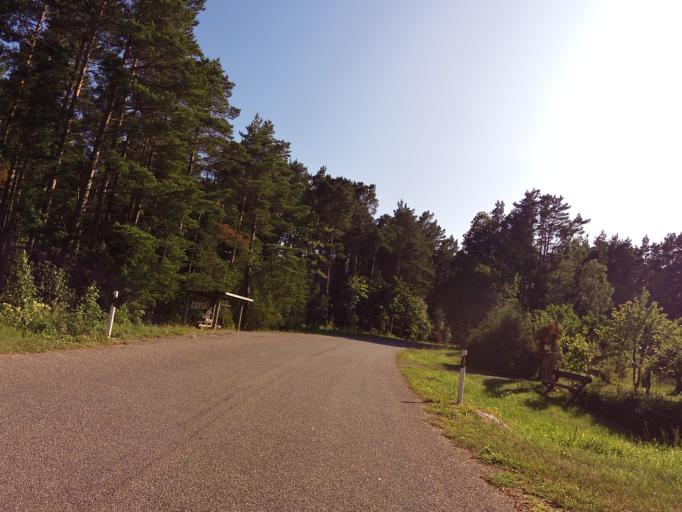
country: EE
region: Hiiumaa
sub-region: Kaerdla linn
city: Kardla
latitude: 58.8922
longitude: 22.2713
